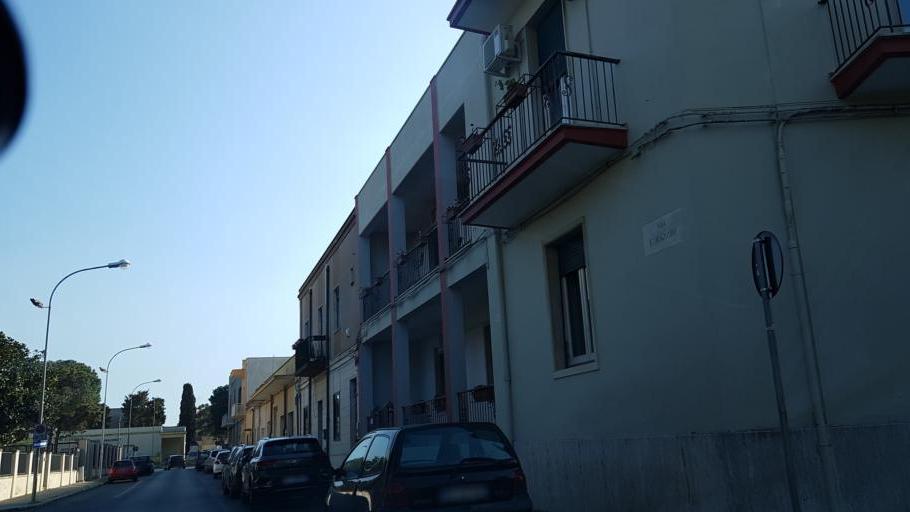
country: IT
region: Apulia
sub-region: Provincia di Brindisi
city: Mesagne
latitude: 40.5609
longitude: 17.7998
